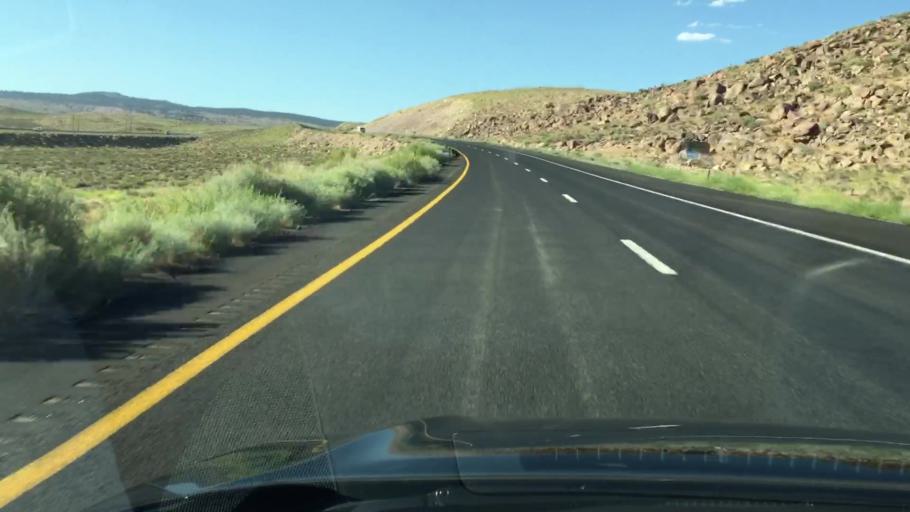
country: US
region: California
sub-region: Inyo County
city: West Bishop
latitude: 37.4663
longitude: -118.5785
